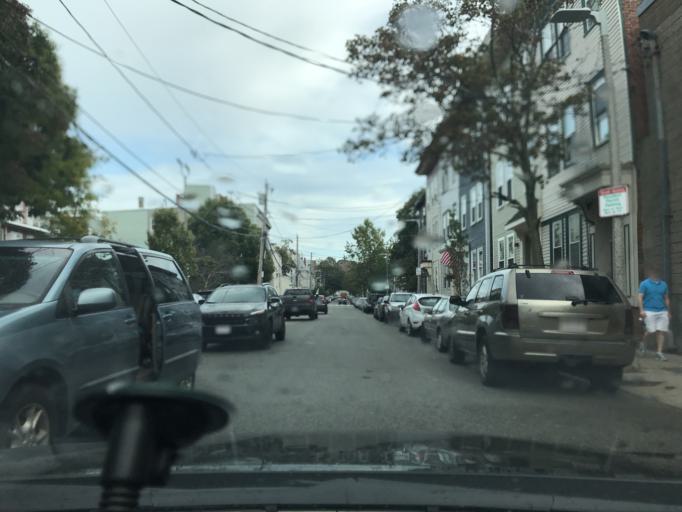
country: US
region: Massachusetts
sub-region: Suffolk County
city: South Boston
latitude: 42.3373
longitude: -71.0521
